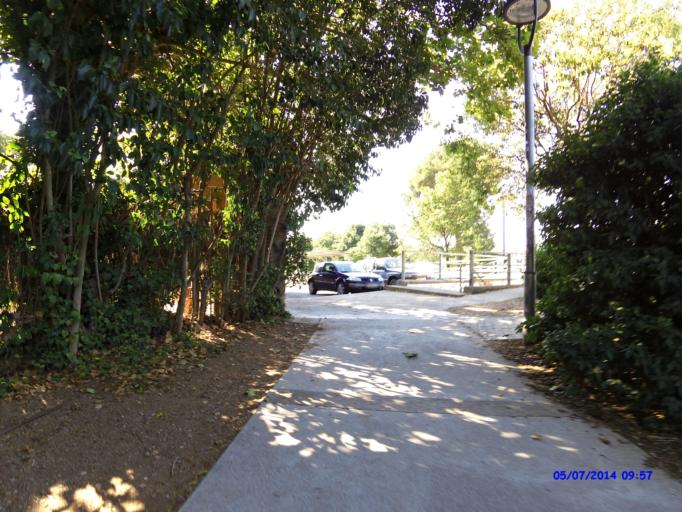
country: ES
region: Catalonia
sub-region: Provincia de Barcelona
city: Rubi
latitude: 41.5279
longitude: 2.0341
